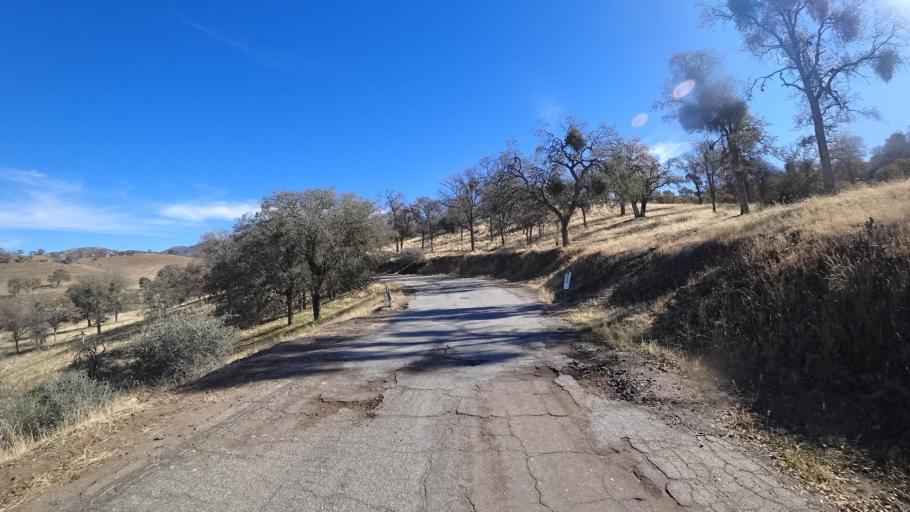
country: US
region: California
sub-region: Kern County
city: Bodfish
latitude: 35.4390
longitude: -118.6975
